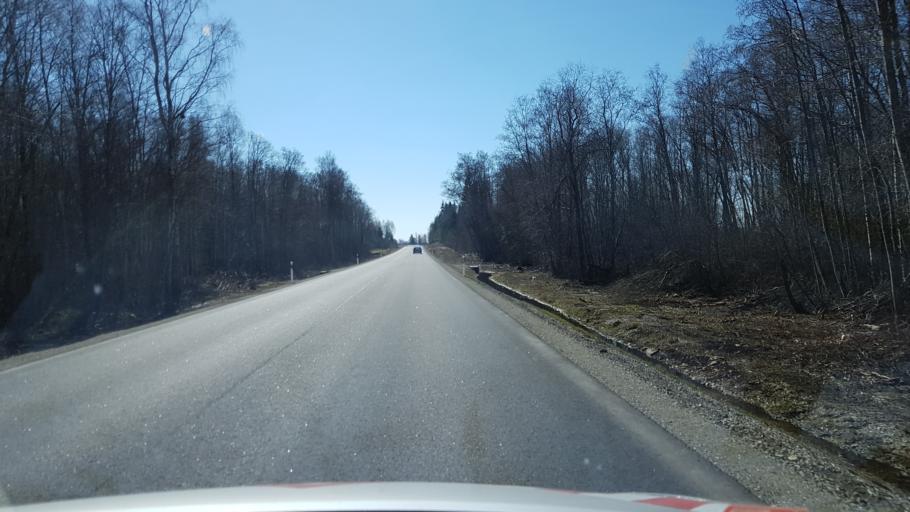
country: EE
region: Laeaene-Virumaa
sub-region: Vinni vald
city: Vinni
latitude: 59.0925
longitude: 26.6233
